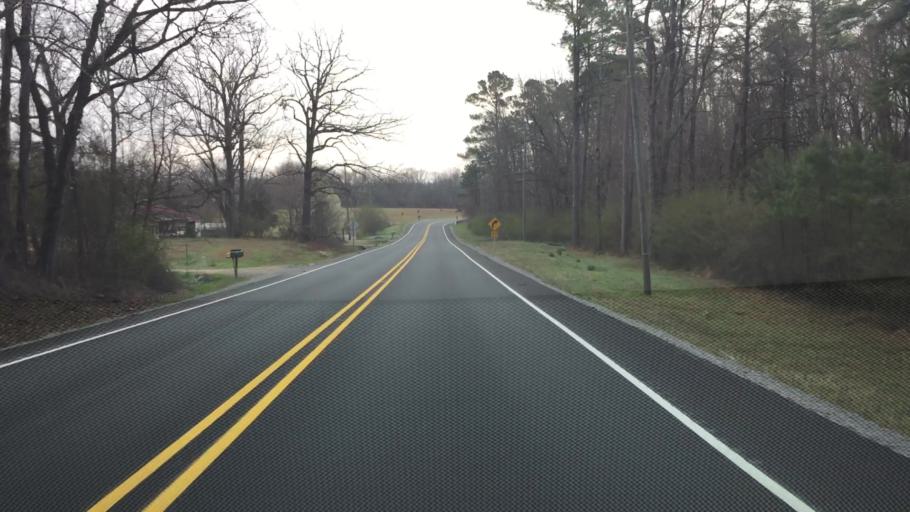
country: US
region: Arkansas
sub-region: Saline County
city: Haskell
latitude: 34.6162
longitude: -92.7835
